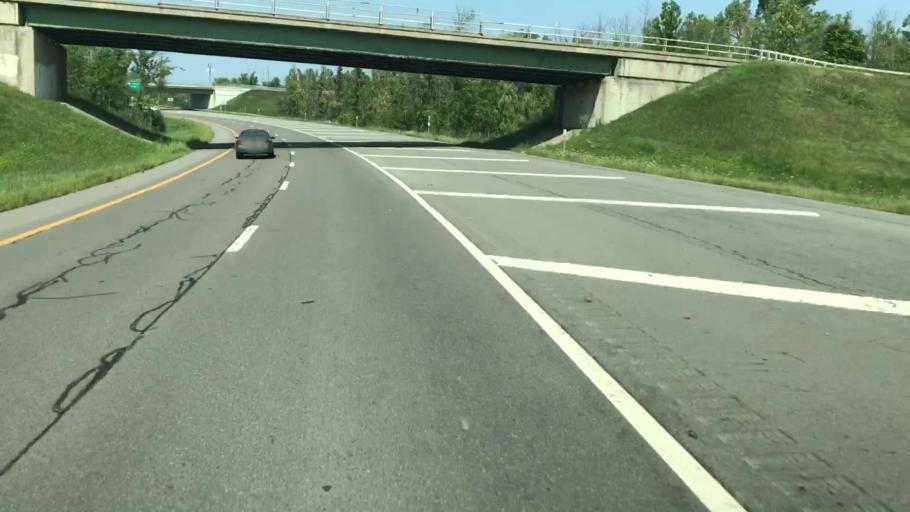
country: US
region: New York
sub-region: Onondaga County
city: East Syracuse
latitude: 43.0549
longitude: -76.0516
